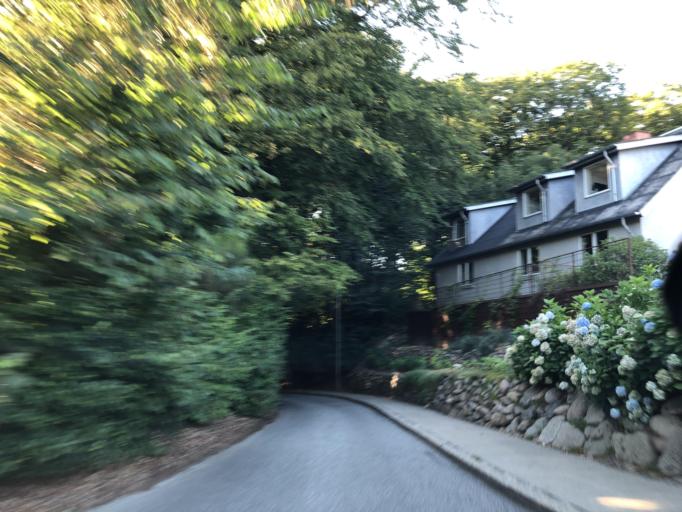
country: DK
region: North Denmark
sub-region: Mariagerfjord Kommune
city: Hobro
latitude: 56.6337
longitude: 9.8248
